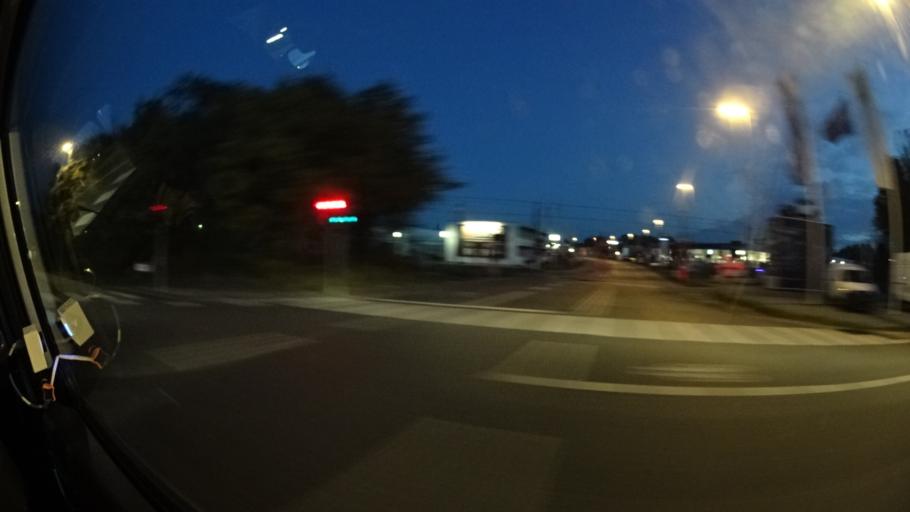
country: DK
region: South Denmark
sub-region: Odense Kommune
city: Hojby
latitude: 55.3397
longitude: 10.4413
